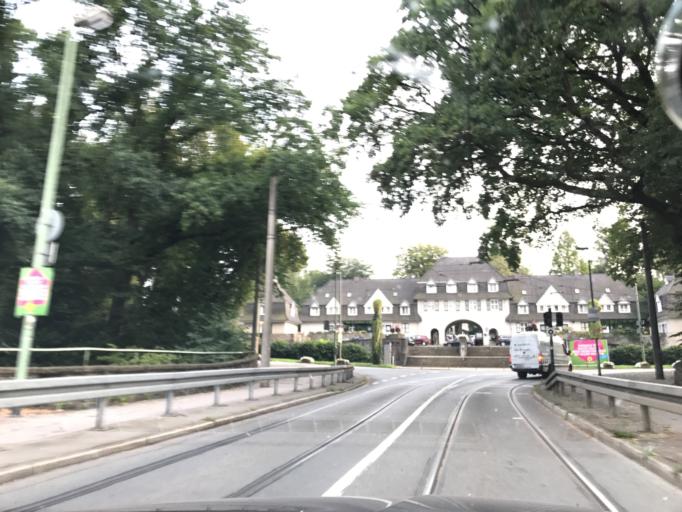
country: DE
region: North Rhine-Westphalia
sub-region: Regierungsbezirk Dusseldorf
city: Essen
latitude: 51.4351
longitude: 6.9796
